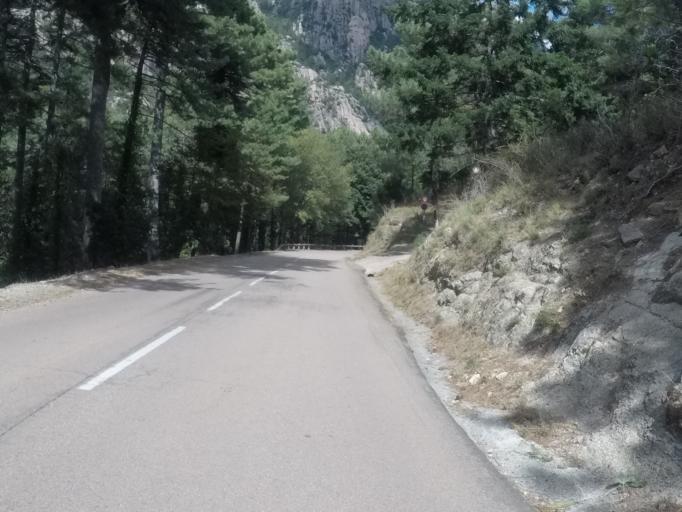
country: FR
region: Corsica
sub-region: Departement de la Corse-du-Sud
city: Zonza
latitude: 41.8109
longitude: 9.2457
